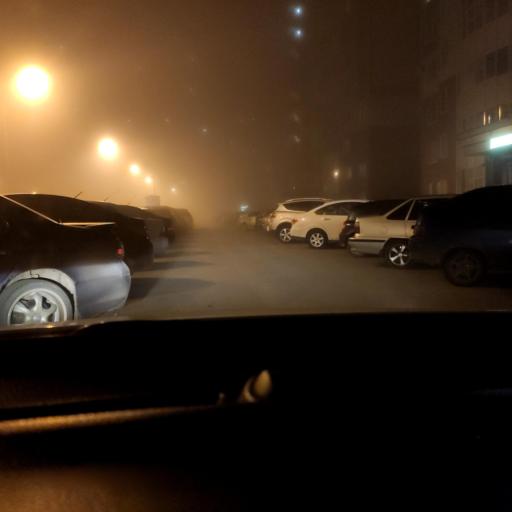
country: RU
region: Voronezj
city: Somovo
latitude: 51.6688
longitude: 39.3194
